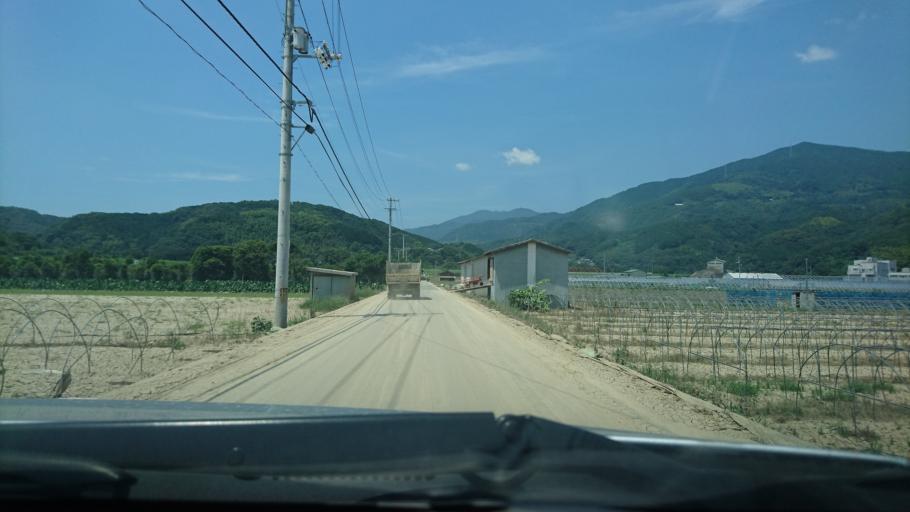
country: JP
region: Ehime
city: Ozu
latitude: 33.5334
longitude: 132.5675
